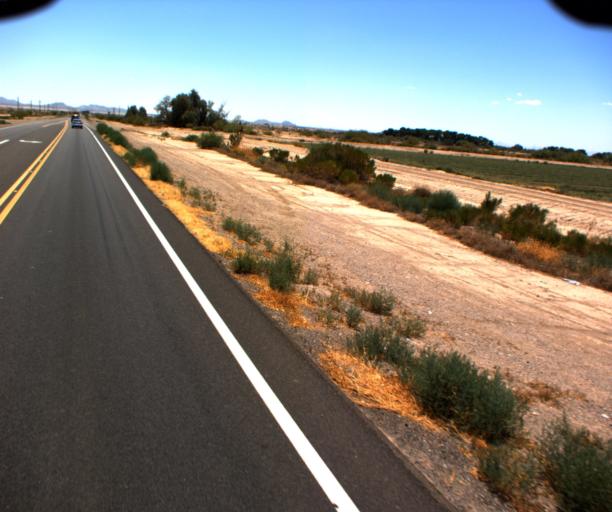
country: US
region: Arizona
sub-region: Maricopa County
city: Sun Lakes
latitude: 33.1606
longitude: -111.8410
